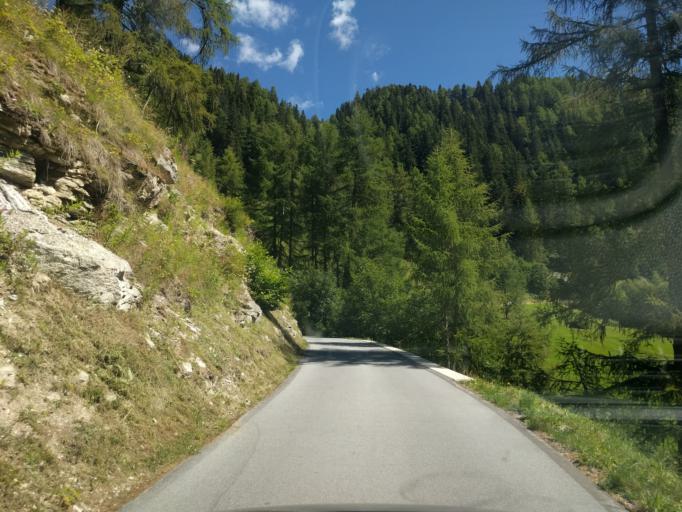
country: IT
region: Trentino-Alto Adige
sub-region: Bolzano
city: Tubre
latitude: 46.6104
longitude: 10.3895
